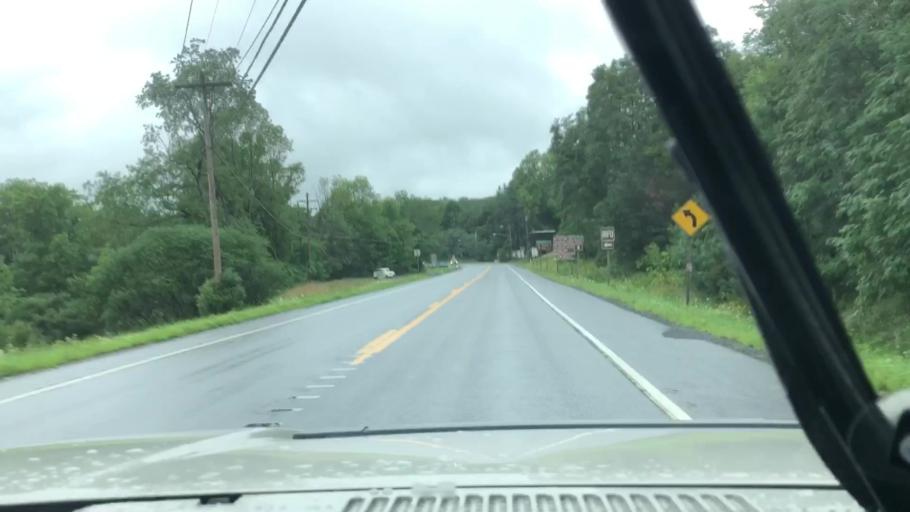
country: US
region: New York
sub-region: Greene County
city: Cairo
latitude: 42.3076
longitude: -74.2288
